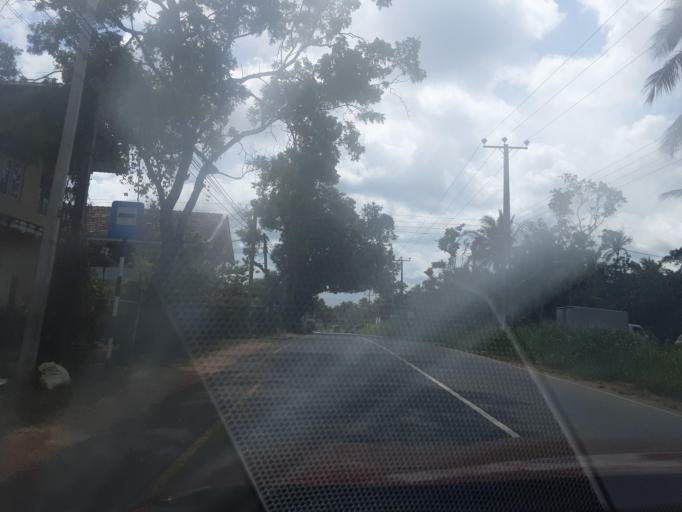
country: LK
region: North Western
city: Kuliyapitiya
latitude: 7.4826
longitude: 79.9853
